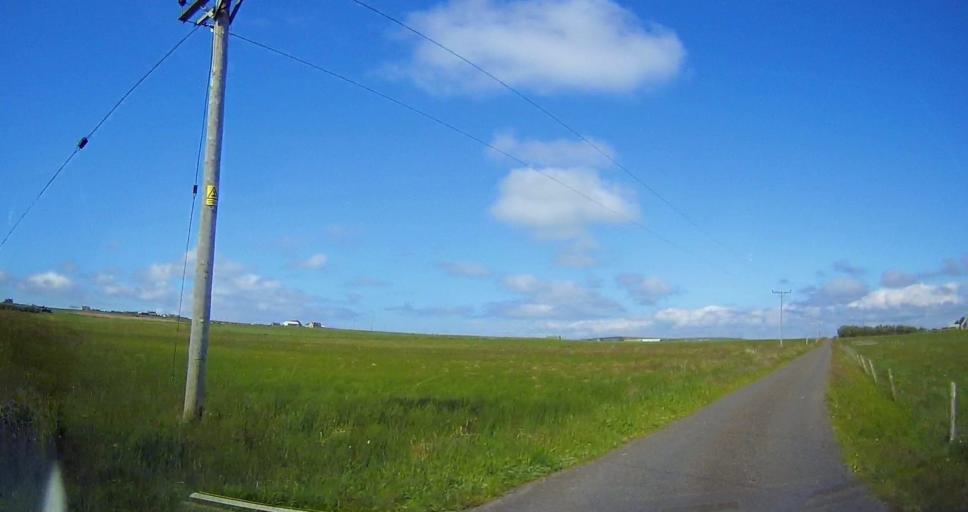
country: GB
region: Scotland
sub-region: Orkney Islands
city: Kirkwall
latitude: 58.8273
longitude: -2.8953
